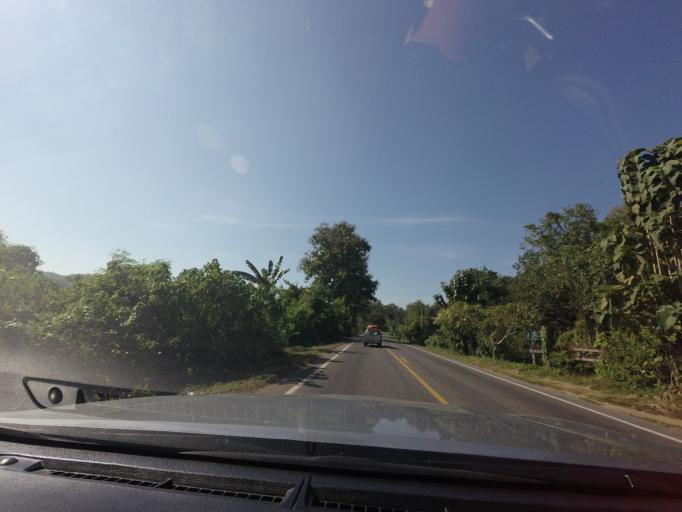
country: TH
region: Sukhothai
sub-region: Amphoe Si Satchanalai
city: Si Satchanalai
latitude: 17.6073
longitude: 99.7088
